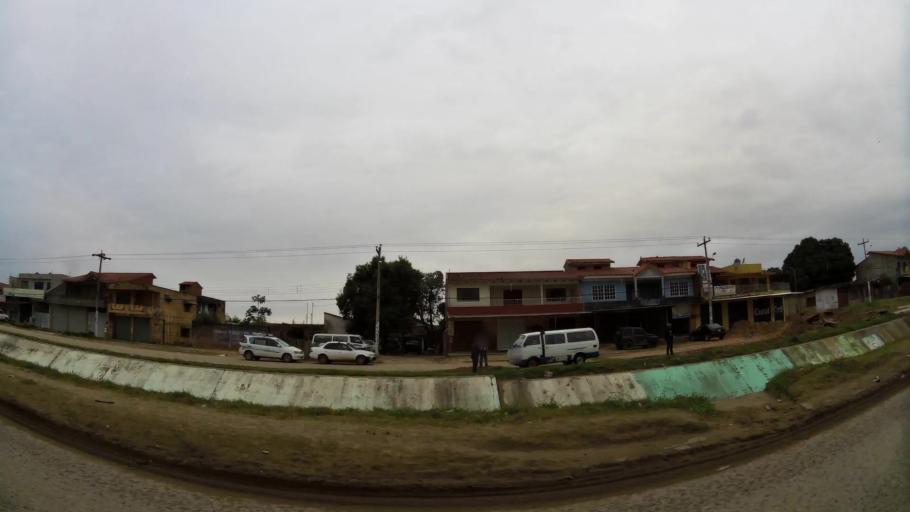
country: BO
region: Santa Cruz
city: Santa Cruz de la Sierra
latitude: -17.8541
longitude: -63.1798
